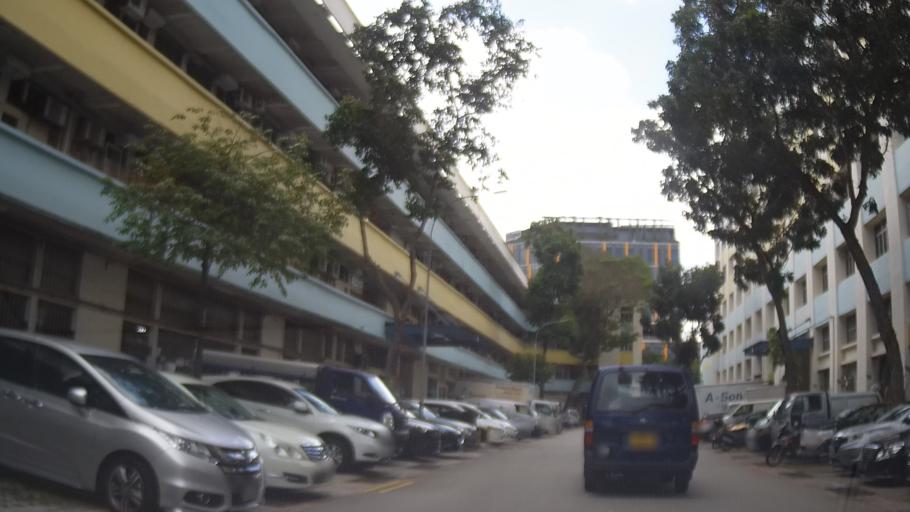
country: SG
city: Singapore
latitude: 1.3191
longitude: 103.8903
